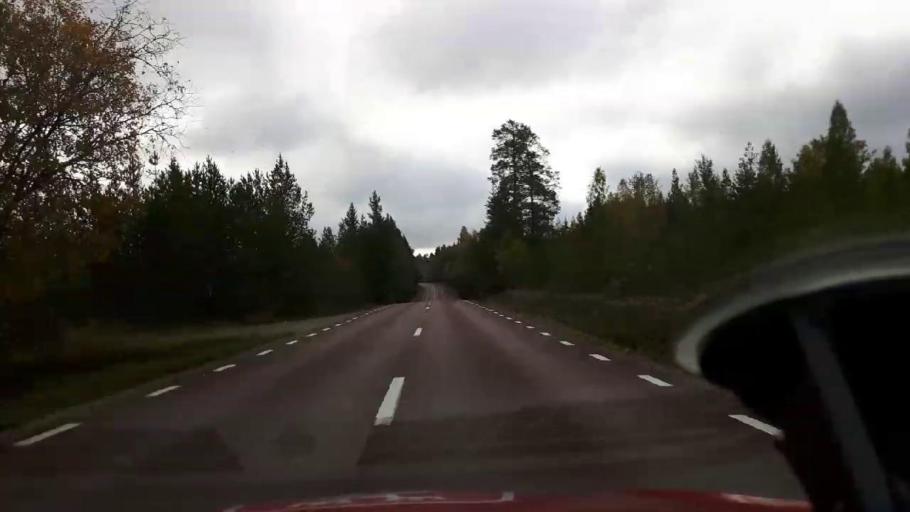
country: SE
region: Jaemtland
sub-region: Harjedalens Kommun
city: Sveg
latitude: 62.1835
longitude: 14.8739
